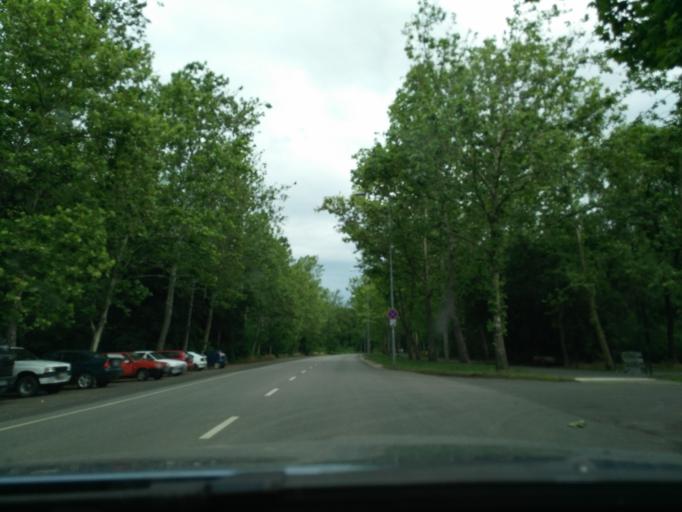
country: HU
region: Hajdu-Bihar
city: Debrecen
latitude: 47.5560
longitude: 21.6334
